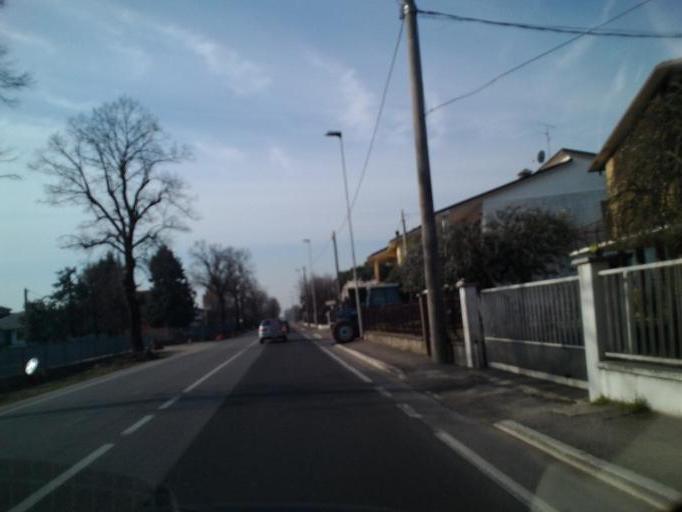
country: IT
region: Veneto
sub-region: Provincia di Verona
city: Mozzecane
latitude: 45.3025
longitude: 10.8124
